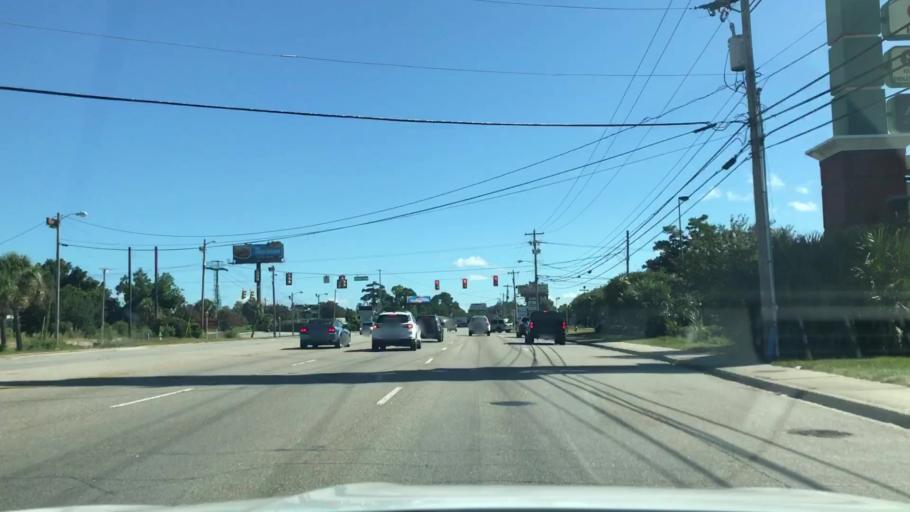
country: US
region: South Carolina
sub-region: Horry County
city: North Myrtle Beach
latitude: 33.7802
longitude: -78.7902
